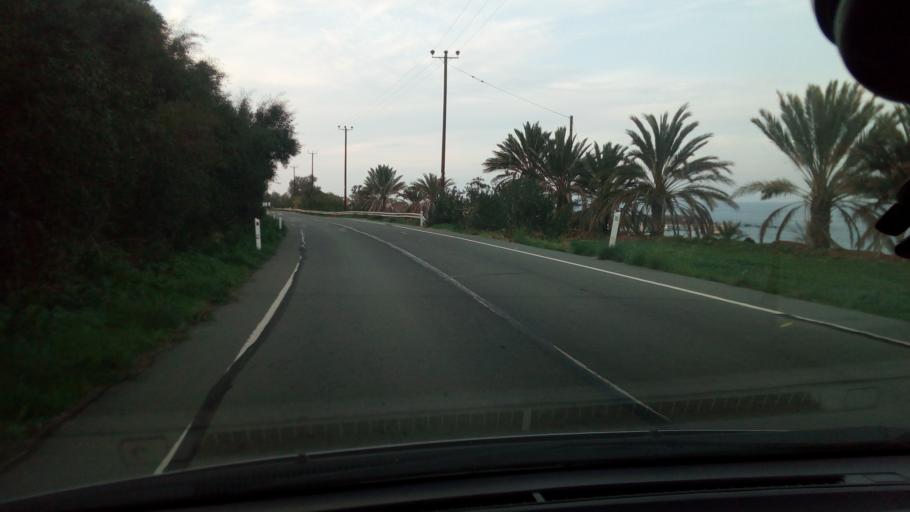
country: CY
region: Lefkosia
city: Kato Pyrgos
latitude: 35.1709
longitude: 32.5572
